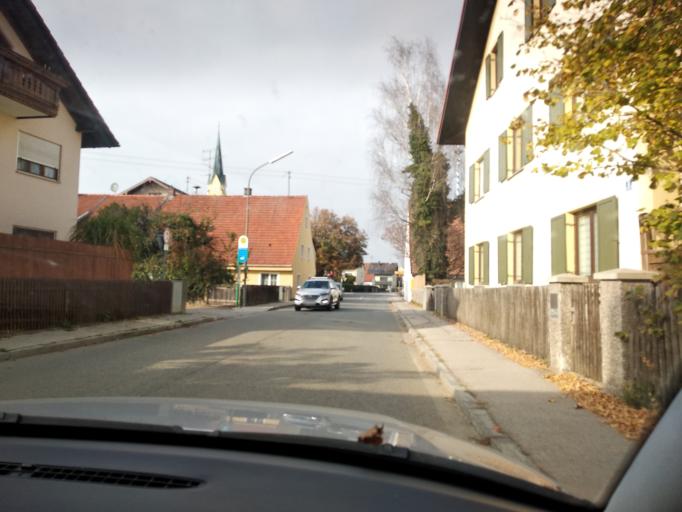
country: DE
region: Bavaria
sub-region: Upper Bavaria
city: Poing
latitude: 48.1473
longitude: 11.8194
